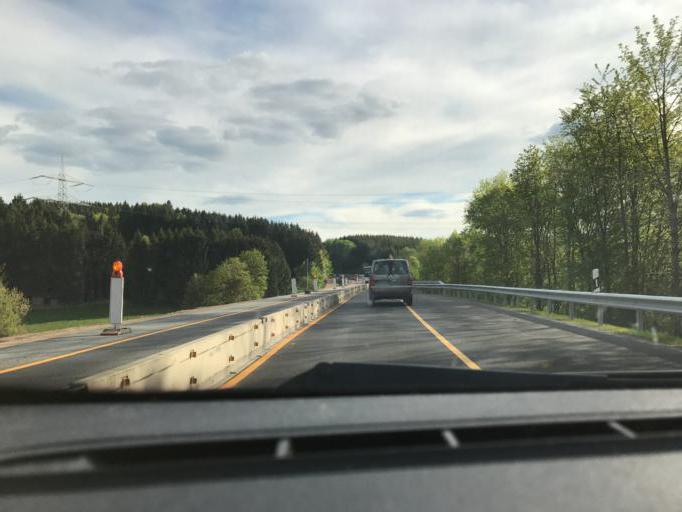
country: DE
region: Rheinland-Pfalz
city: Weinsheim
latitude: 50.2304
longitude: 6.4530
